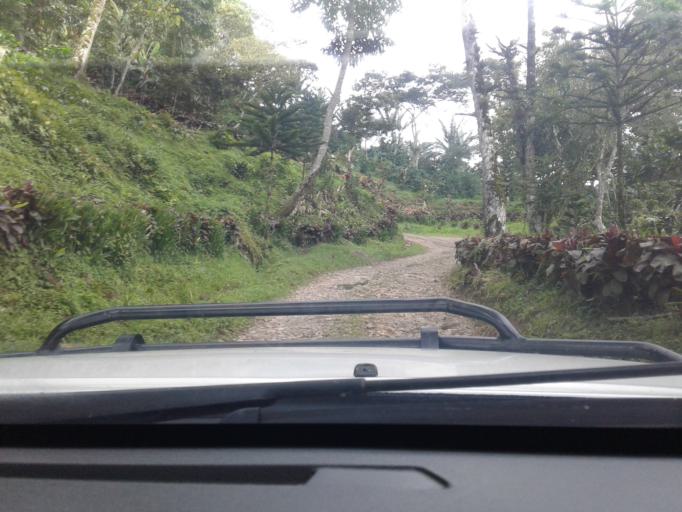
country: NI
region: Jinotega
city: Jinotega
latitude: 13.0691
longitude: -85.8805
